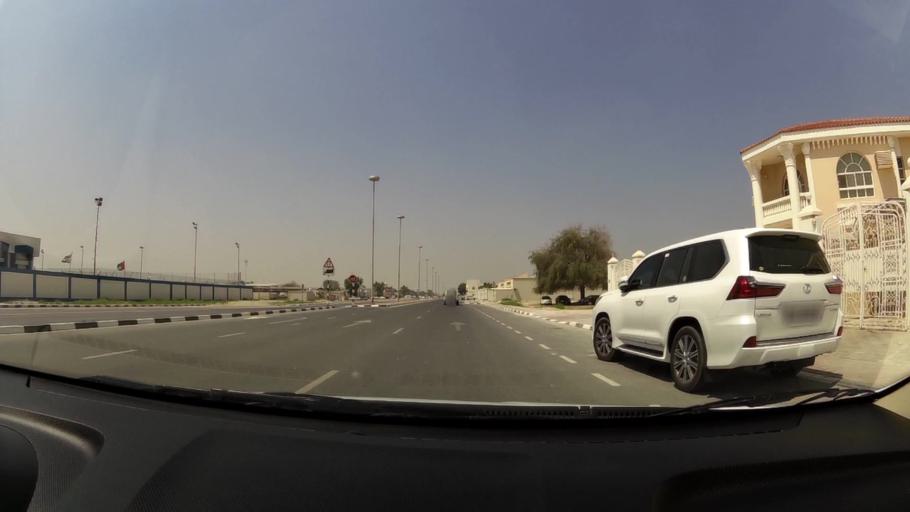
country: AE
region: Umm al Qaywayn
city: Umm al Qaywayn
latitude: 25.5668
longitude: 55.5578
